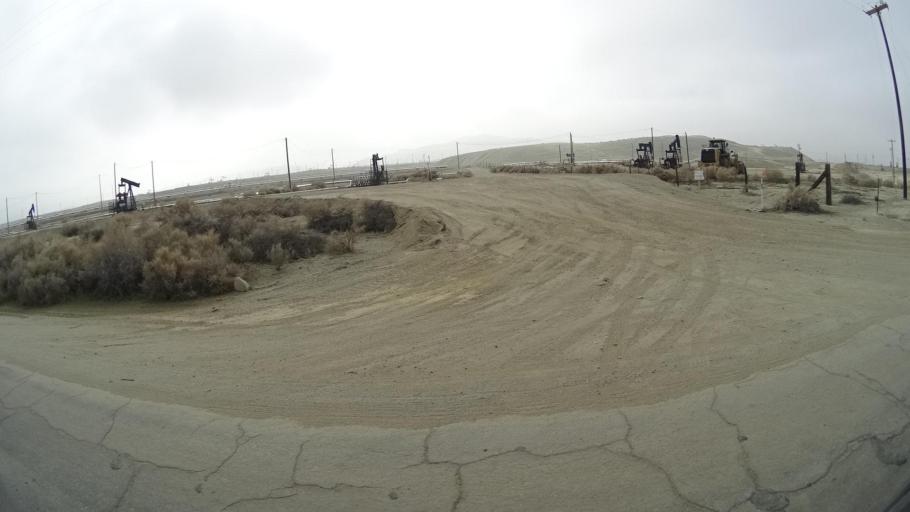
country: US
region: California
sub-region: Kern County
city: Maricopa
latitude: 35.0361
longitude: -119.3557
